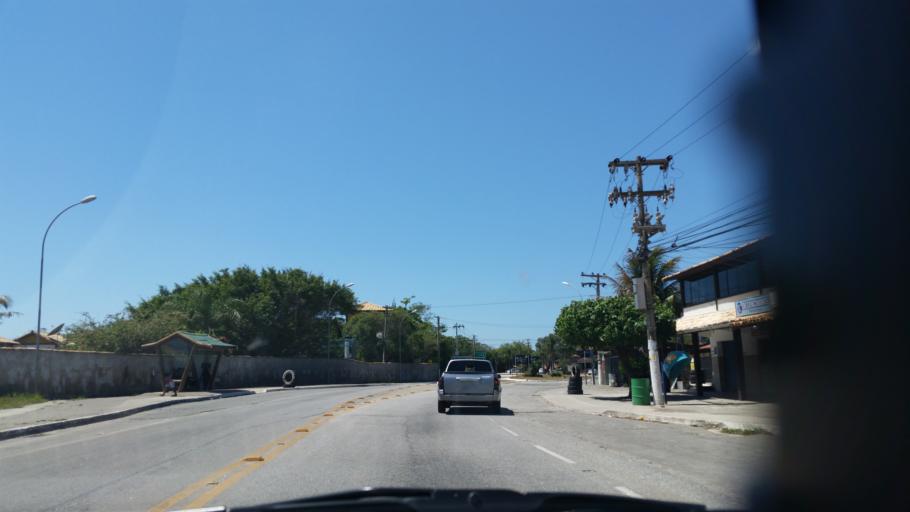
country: BR
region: Rio de Janeiro
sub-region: Armacao De Buzios
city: Armacao de Buzios
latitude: -22.7751
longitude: -41.9317
